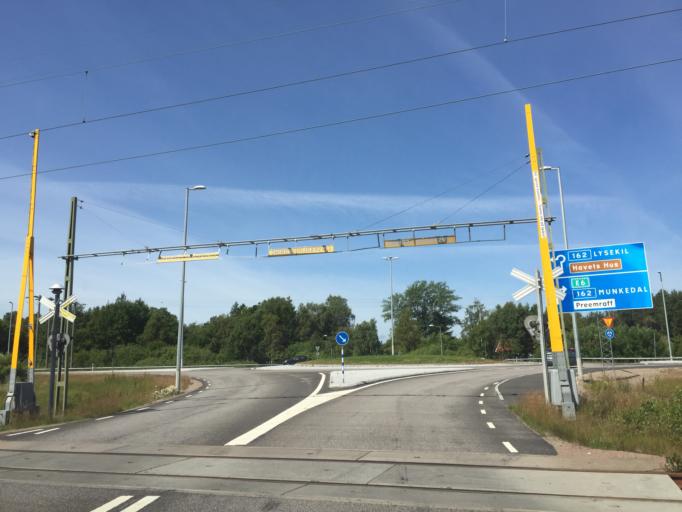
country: SE
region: Vaestra Goetaland
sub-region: Lysekils Kommun
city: Lysekil
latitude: 58.3034
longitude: 11.4772
